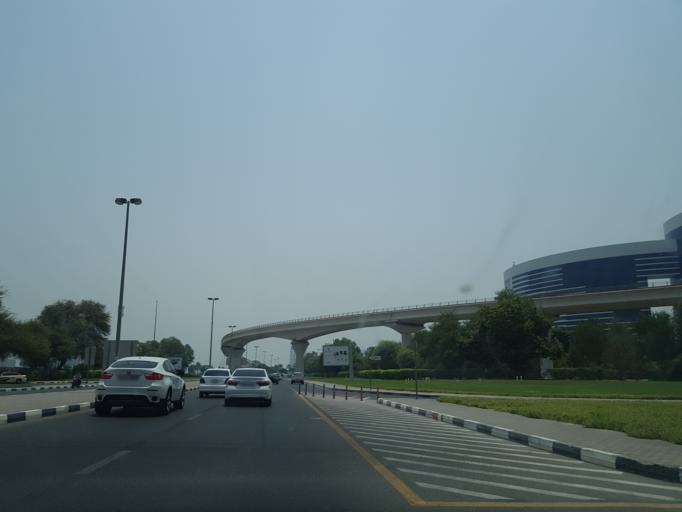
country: AE
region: Ash Shariqah
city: Sharjah
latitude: 25.2318
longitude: 55.3275
